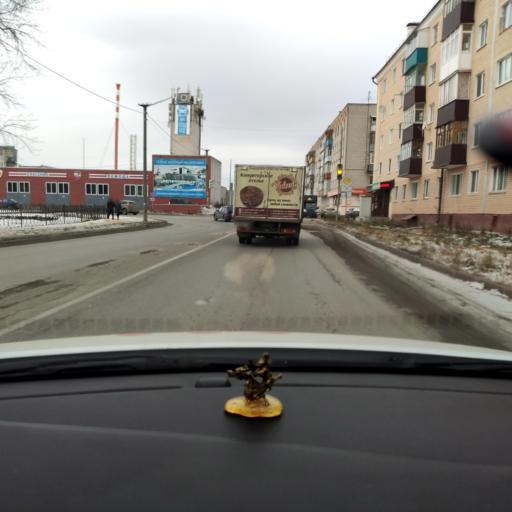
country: RU
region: Tatarstan
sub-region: Zelenodol'skiy Rayon
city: Zelenodolsk
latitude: 55.8562
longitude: 48.5320
